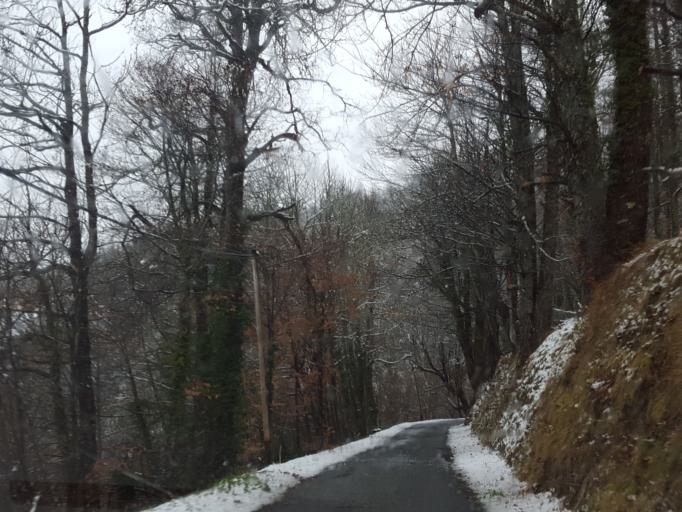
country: FR
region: Midi-Pyrenees
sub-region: Departement de l'Ariege
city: Montjoie-en-Couserans
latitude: 42.9048
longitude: 1.3530
